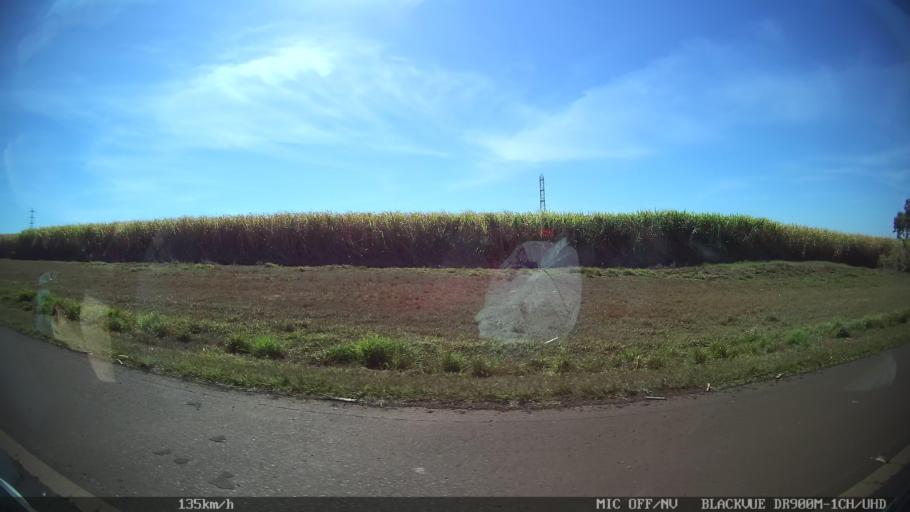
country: BR
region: Sao Paulo
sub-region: Ipua
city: Ipua
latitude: -20.4495
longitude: -48.1864
